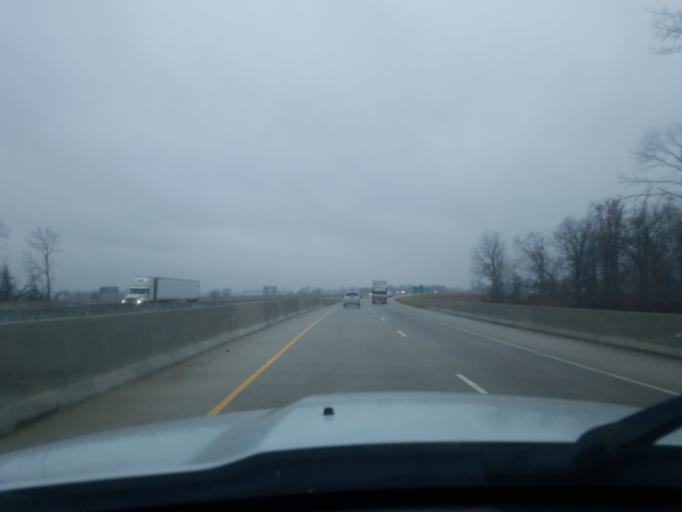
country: US
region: Indiana
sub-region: Howard County
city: Indian Heights
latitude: 40.4409
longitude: -86.0773
